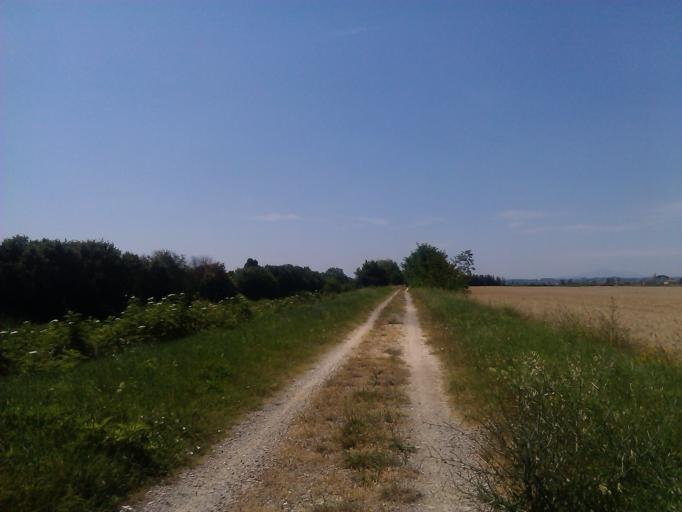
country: IT
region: Tuscany
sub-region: Province of Arezzo
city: Cesa
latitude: 43.3572
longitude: 11.8267
